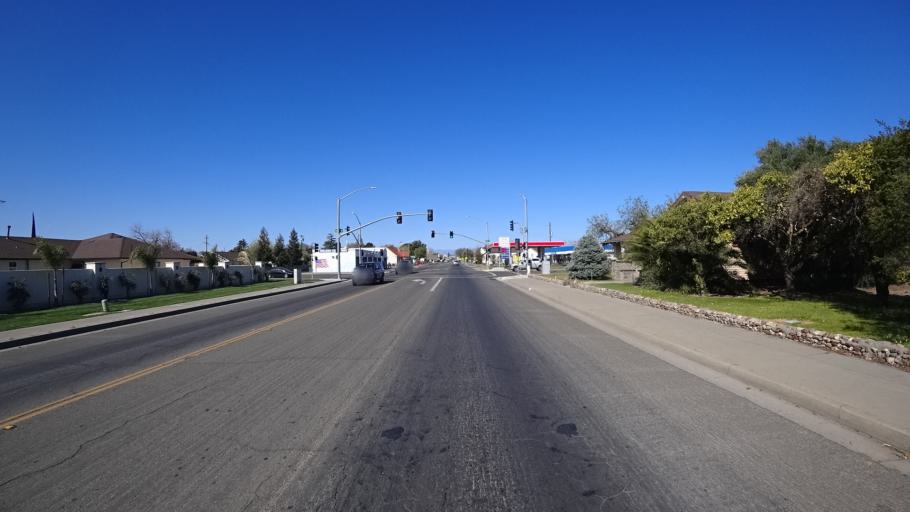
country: US
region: California
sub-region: Glenn County
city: Orland
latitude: 39.7474
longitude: -122.1869
